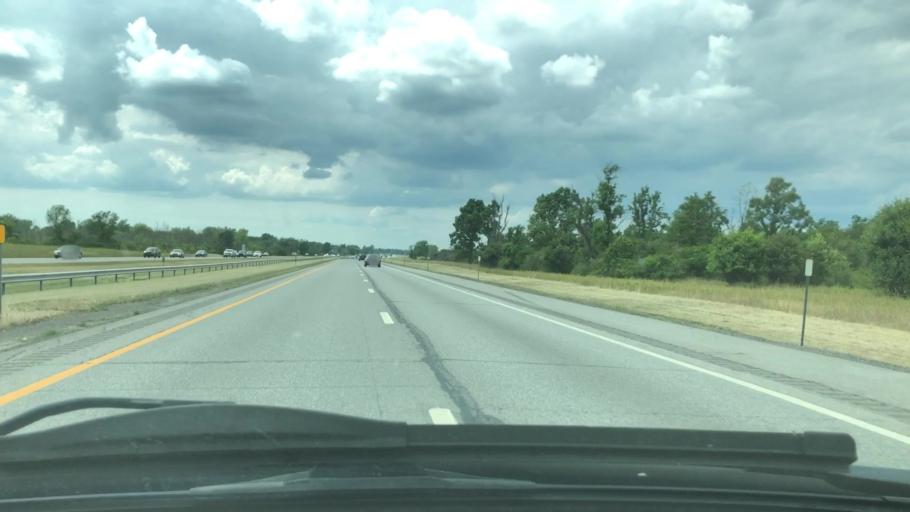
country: US
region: New York
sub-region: Erie County
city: Harris Hill
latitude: 42.9490
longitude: -78.6370
